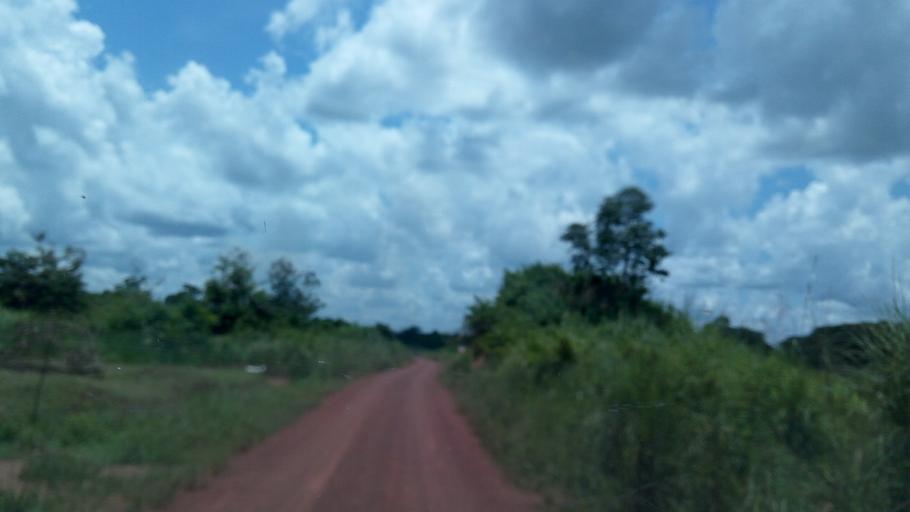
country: CD
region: Equateur
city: Libenge
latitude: 3.7716
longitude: 18.9506
